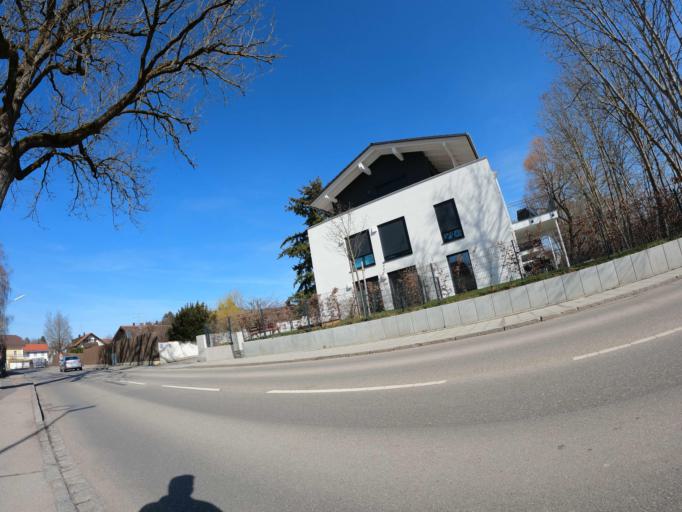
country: DE
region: Bavaria
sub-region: Upper Bavaria
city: Taufkirchen
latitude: 48.0421
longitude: 11.6186
